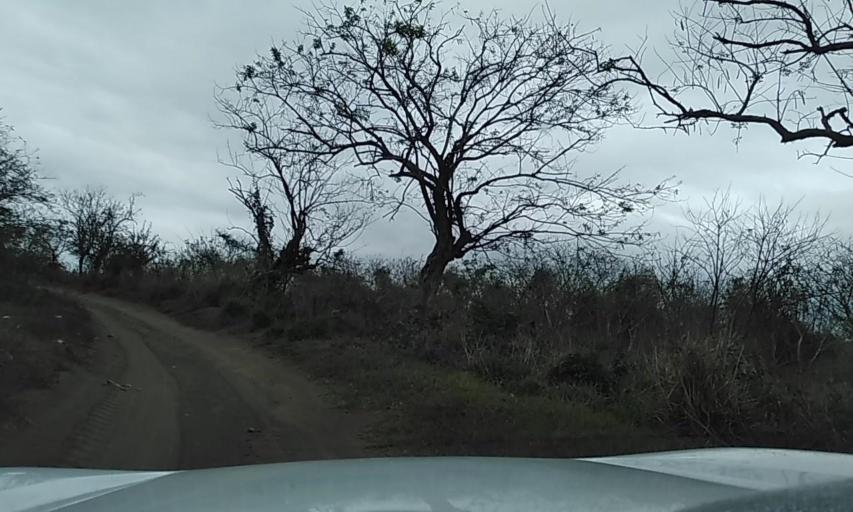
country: MX
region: Veracruz
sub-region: Veracruz
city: Delfino Victoria (Santa Fe)
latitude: 19.2705
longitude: -96.3076
